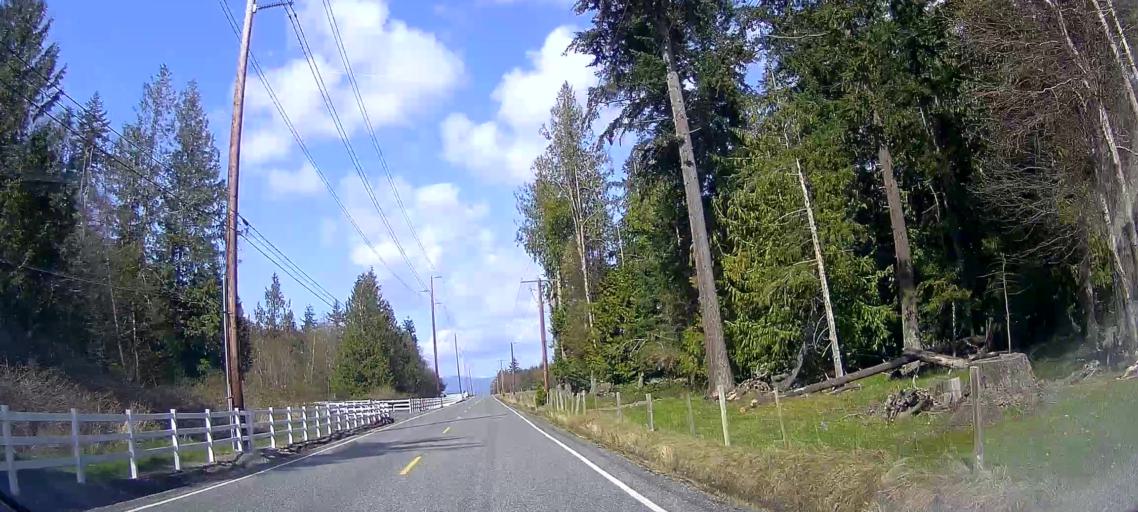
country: US
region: Washington
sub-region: Skagit County
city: Burlington
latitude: 48.4962
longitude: -122.4444
